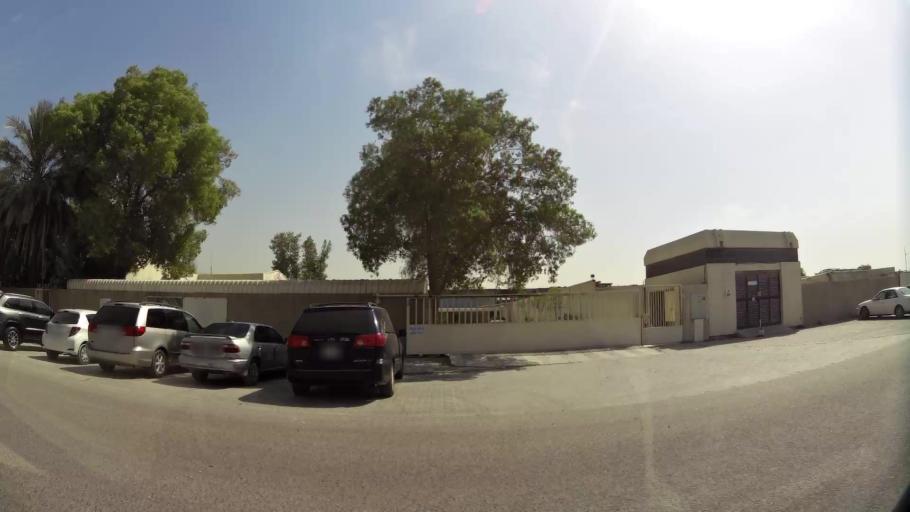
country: AE
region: Ash Shariqah
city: Sharjah
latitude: 25.2789
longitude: 55.3914
